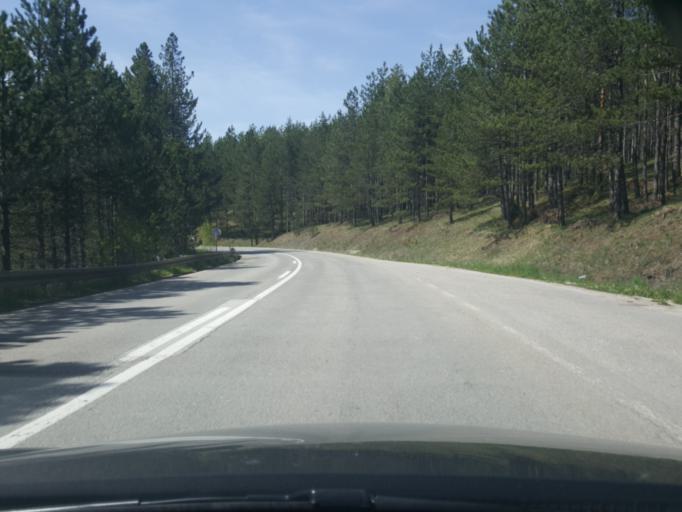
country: RS
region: Central Serbia
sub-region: Zlatiborski Okrug
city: Cajetina
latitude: 43.8317
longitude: 19.6394
